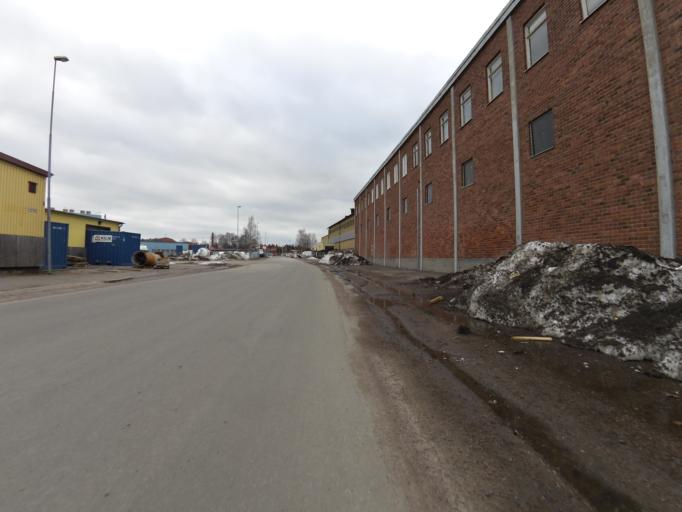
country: SE
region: Gaevleborg
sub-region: Gavle Kommun
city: Gavle
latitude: 60.6686
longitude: 17.1733
